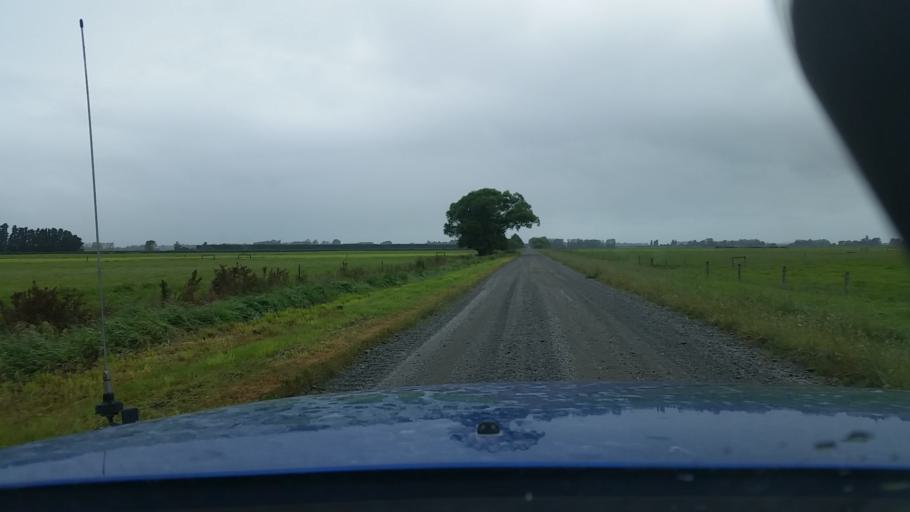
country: NZ
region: Canterbury
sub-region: Ashburton District
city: Tinwald
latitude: -44.0001
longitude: 171.6511
